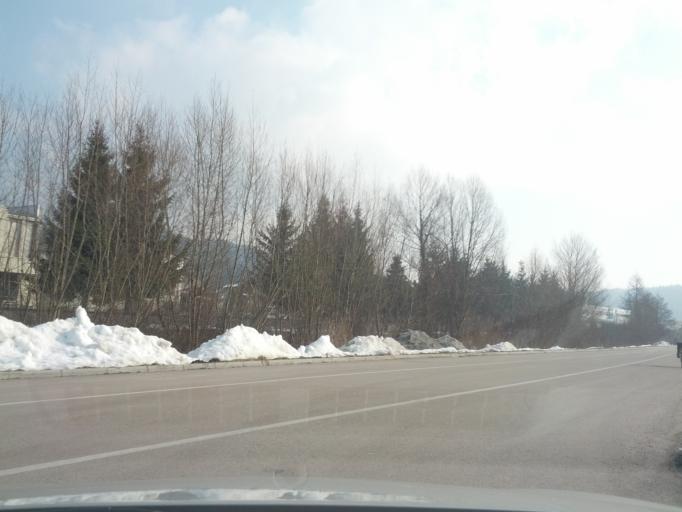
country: SI
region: Skofljica
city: Lavrica
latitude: 46.0234
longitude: 14.5384
